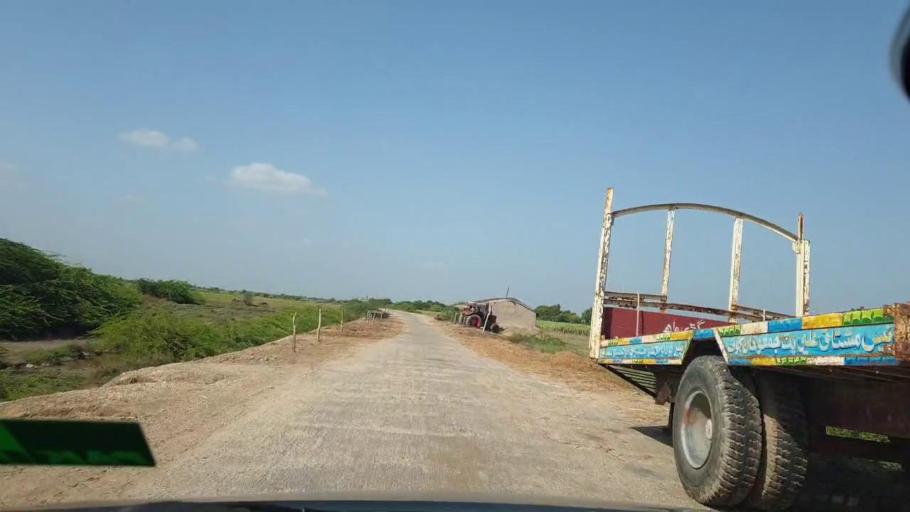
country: PK
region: Sindh
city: Tando Bago
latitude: 24.6869
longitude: 69.1878
